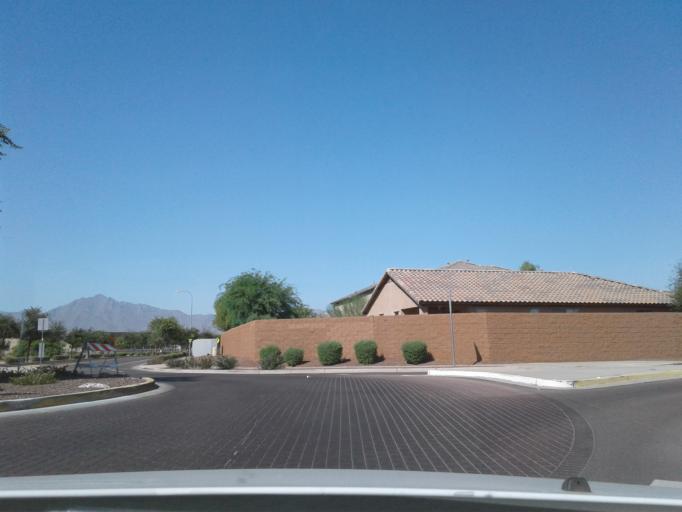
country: US
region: Arizona
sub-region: Maricopa County
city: Laveen
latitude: 33.3748
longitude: -112.2032
